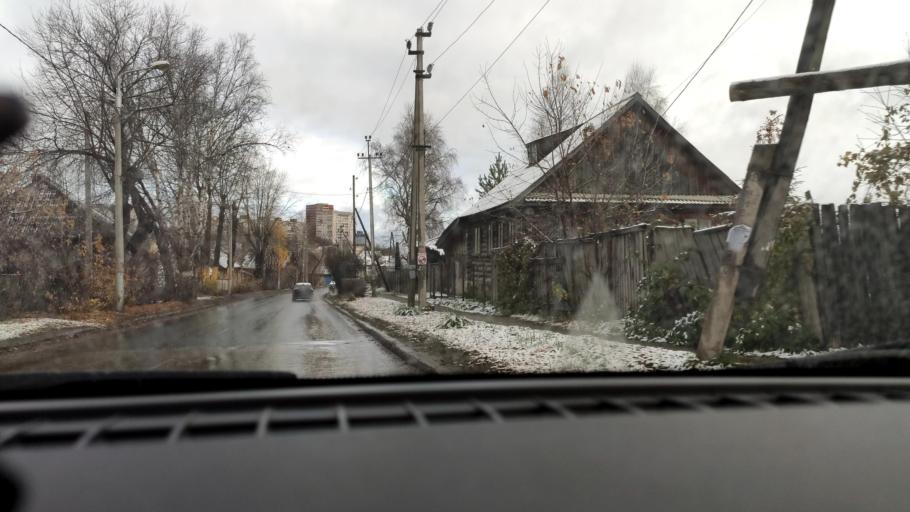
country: RU
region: Perm
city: Perm
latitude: 58.0227
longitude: 56.3127
